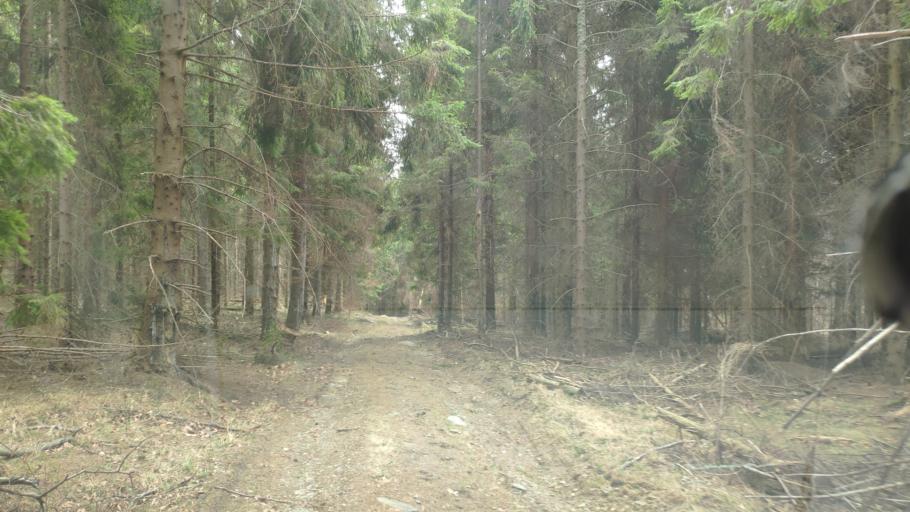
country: SK
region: Kosicky
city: Gelnica
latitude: 48.7595
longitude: 21.0175
